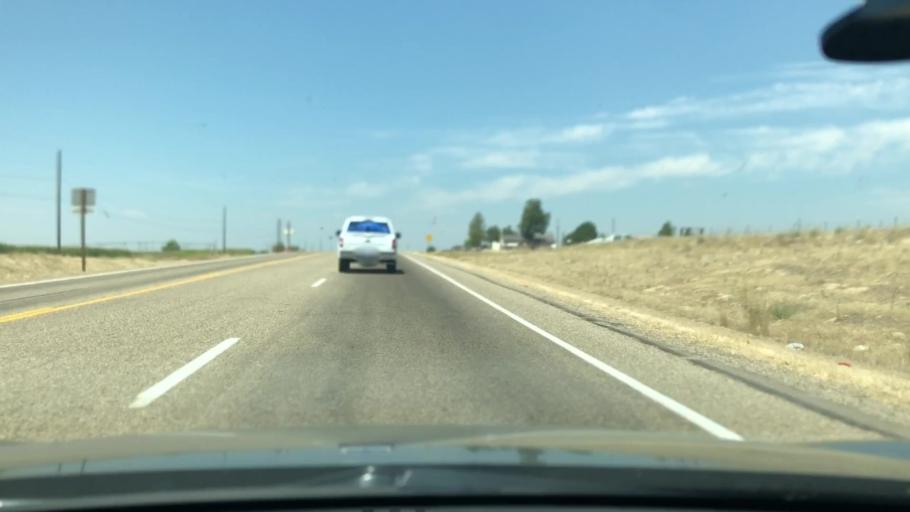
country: US
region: Idaho
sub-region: Canyon County
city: Parma
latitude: 43.8229
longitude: -116.9543
